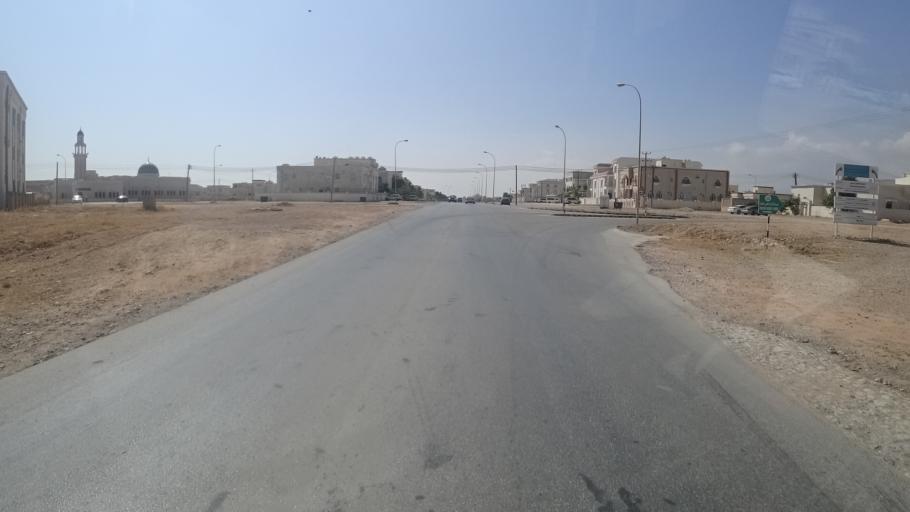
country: OM
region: Zufar
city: Salalah
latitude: 17.0187
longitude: 54.0307
